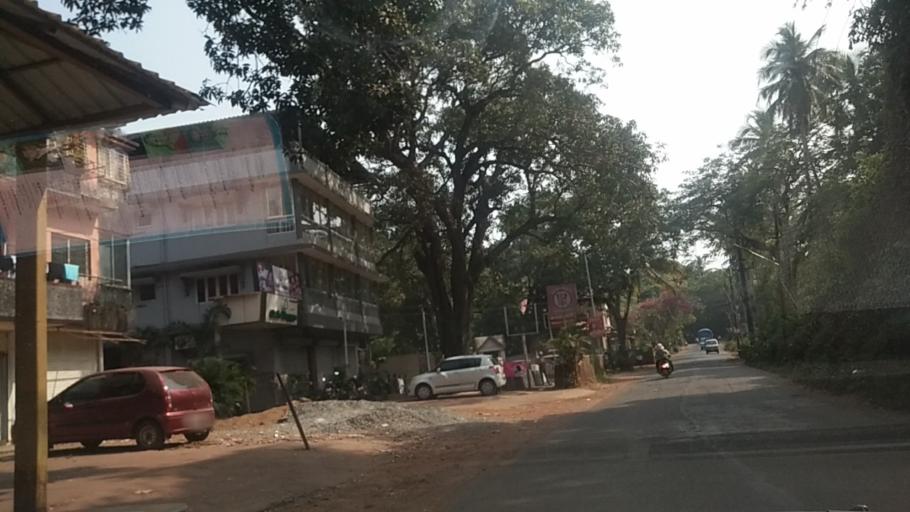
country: IN
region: Goa
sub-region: North Goa
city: Panaji
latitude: 15.5086
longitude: 73.8238
